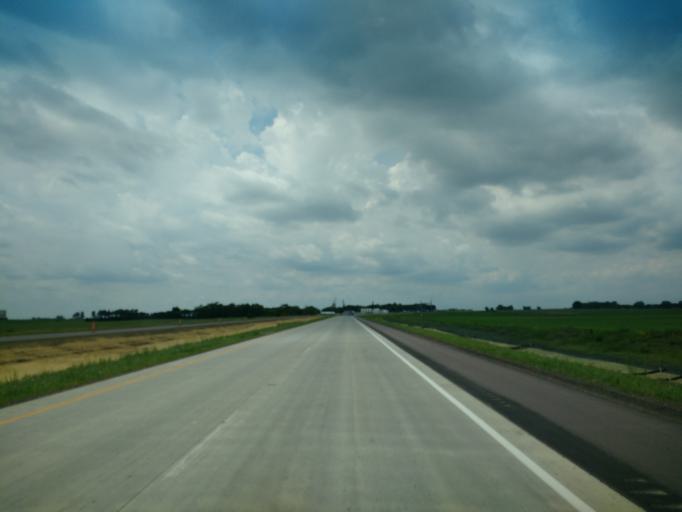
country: US
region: Minnesota
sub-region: Cottonwood County
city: Mountain Lake
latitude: 43.9120
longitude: -95.0249
